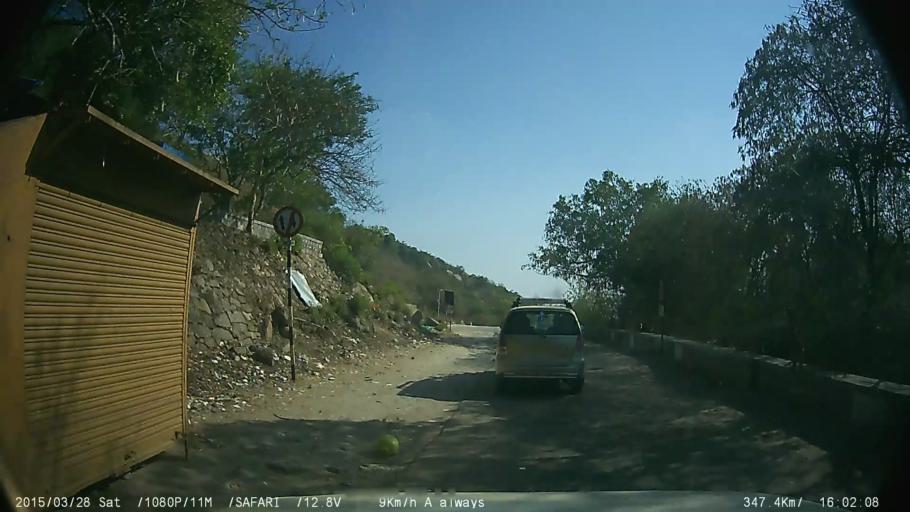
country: IN
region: Karnataka
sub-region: Mysore
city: Mysore
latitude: 12.2795
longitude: 76.6678
